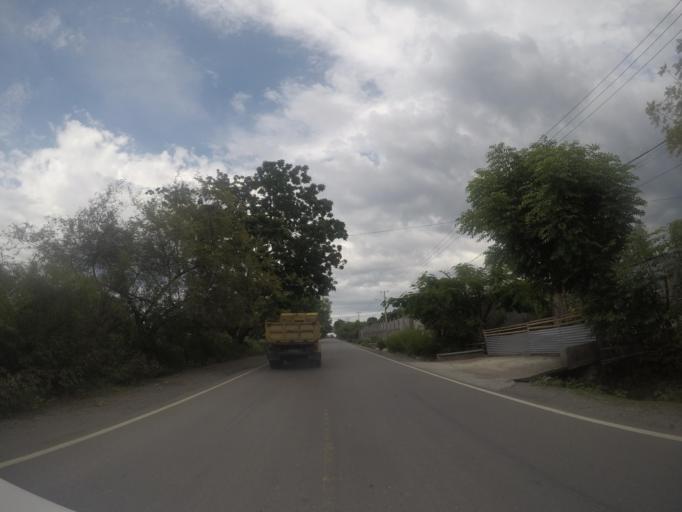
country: TL
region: Liquica
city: Liquica
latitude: -8.6021
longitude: 125.3027
